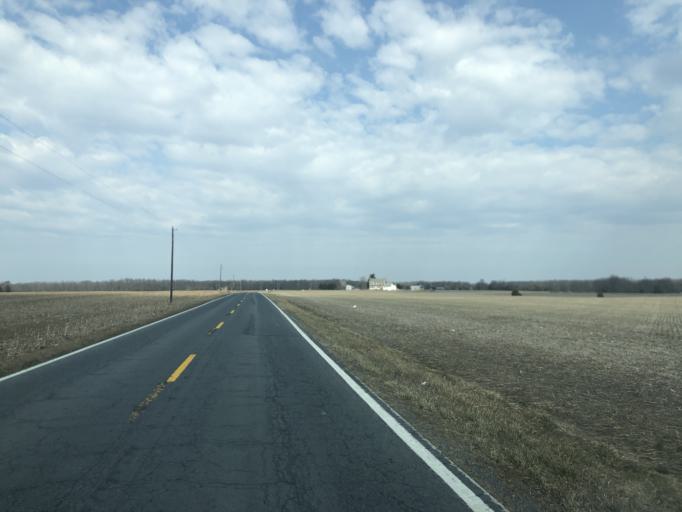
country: US
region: Maryland
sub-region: Caroline County
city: Ridgely
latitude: 39.0417
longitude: -75.9126
